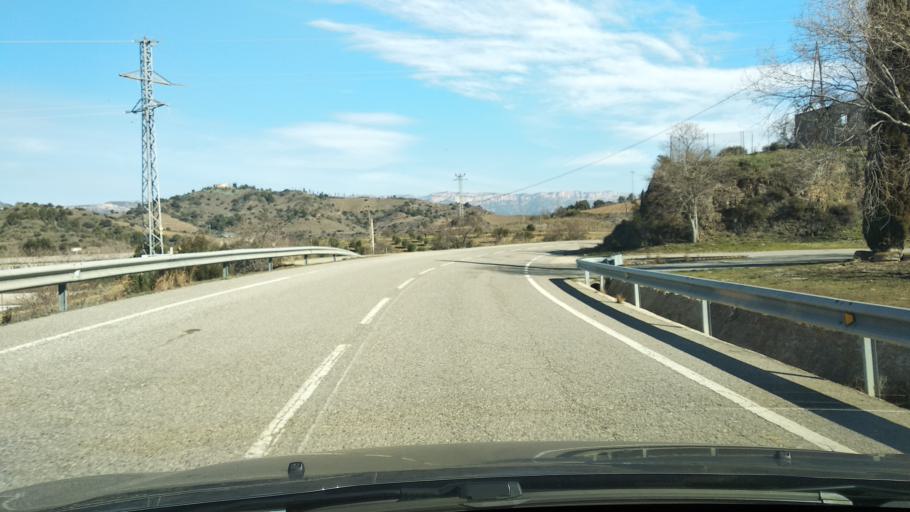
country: ES
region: Catalonia
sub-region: Provincia de Tarragona
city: Falset
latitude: 41.1947
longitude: 0.7768
